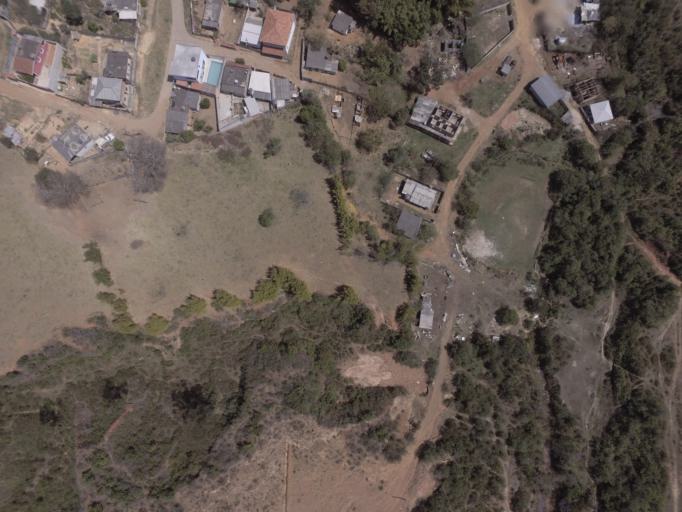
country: BR
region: Minas Gerais
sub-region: Tiradentes
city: Tiradentes
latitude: -21.0497
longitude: -44.0875
